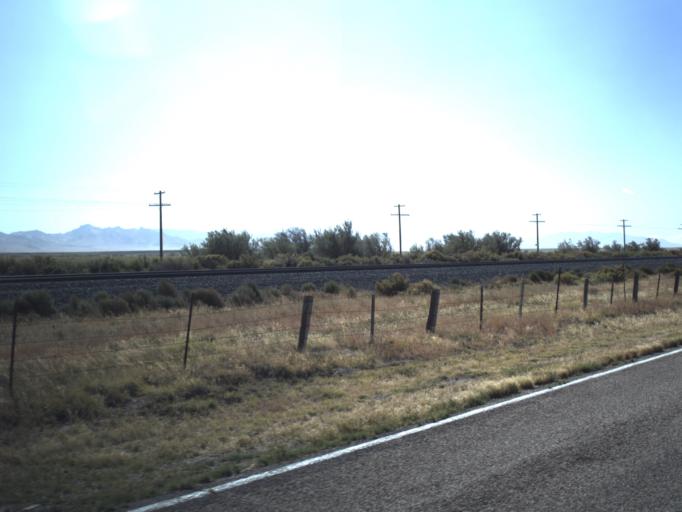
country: US
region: Utah
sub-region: Beaver County
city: Milford
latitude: 38.7113
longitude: -112.9696
